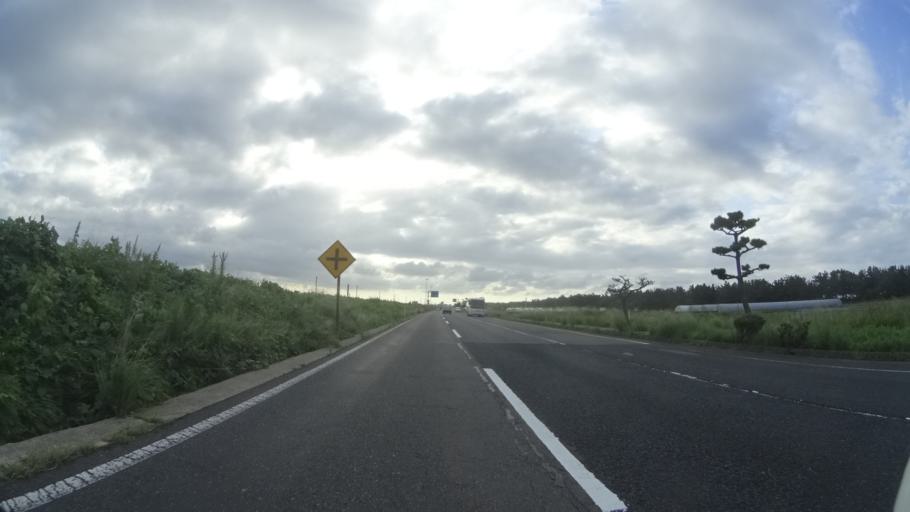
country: JP
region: Tottori
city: Kurayoshi
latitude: 35.4983
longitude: 133.7786
